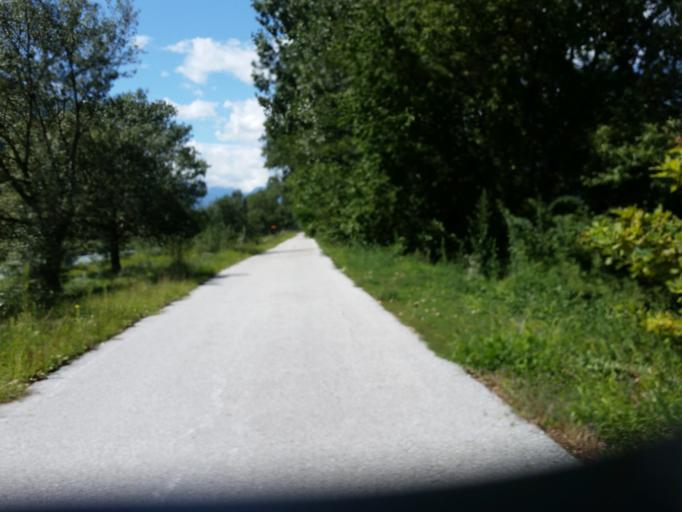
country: CH
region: Valais
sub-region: Conthey District
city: Ardon
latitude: 46.1983
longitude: 7.2788
